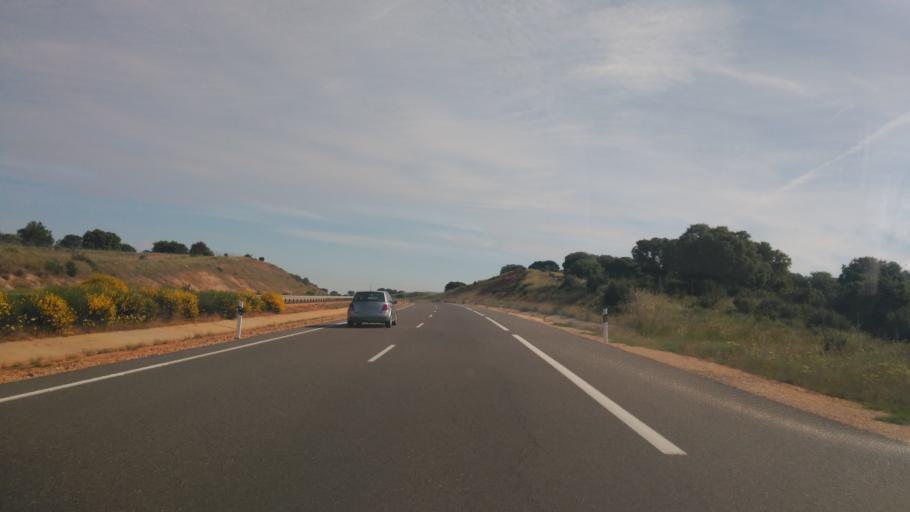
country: ES
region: Castille and Leon
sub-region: Provincia de Zamora
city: Cuelgamures
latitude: 41.2841
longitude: -5.7008
